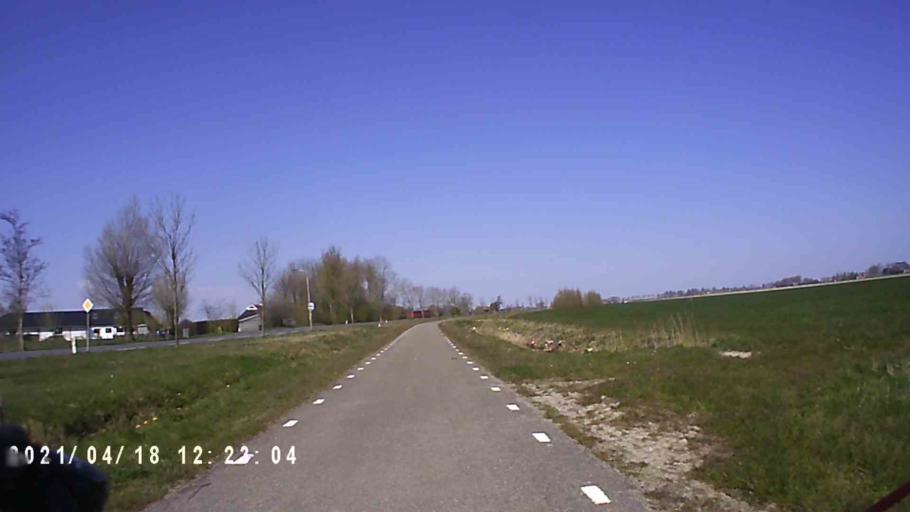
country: NL
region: Friesland
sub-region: Gemeente Dongeradeel
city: Anjum
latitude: 53.3244
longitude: 6.1242
